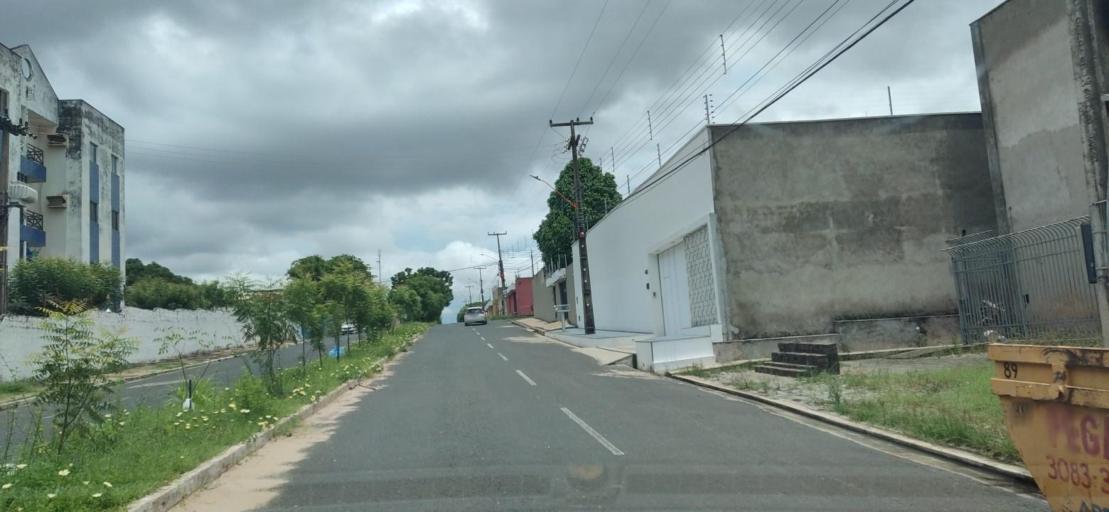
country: BR
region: Piaui
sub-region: Teresina
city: Teresina
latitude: -5.0745
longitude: -42.7567
